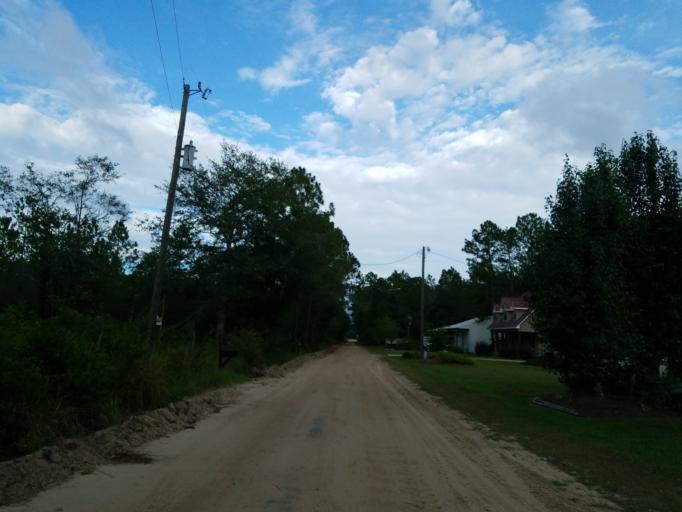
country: US
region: Georgia
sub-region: Cook County
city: Sparks
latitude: 31.2362
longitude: -83.4590
